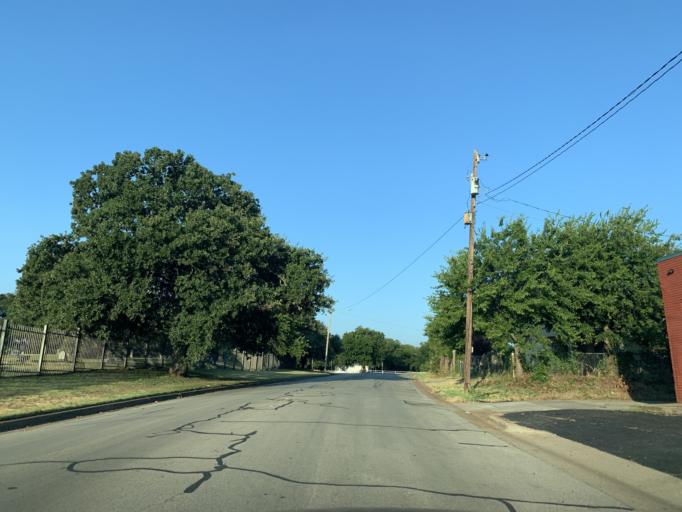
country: US
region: Texas
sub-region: Tarrant County
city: River Oaks
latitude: 32.7726
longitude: -97.3473
